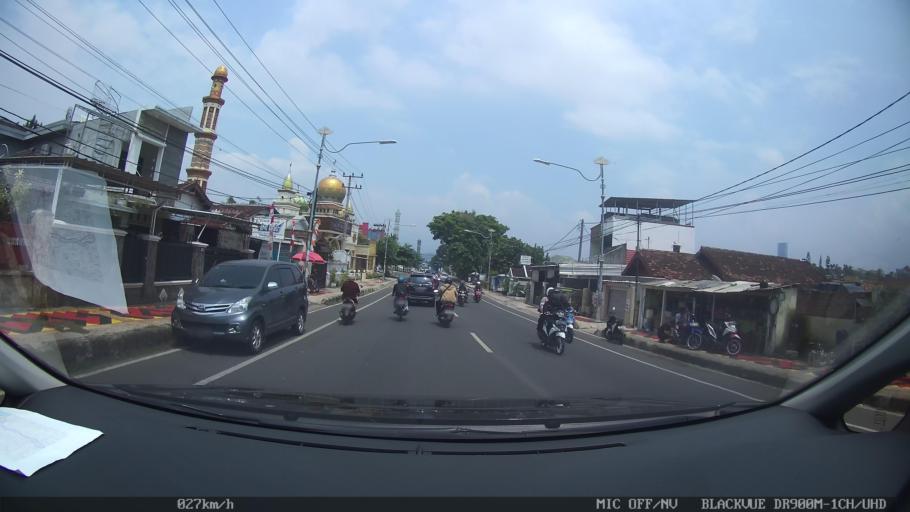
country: ID
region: Lampung
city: Bandarlampung
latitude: -5.4296
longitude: 105.2671
